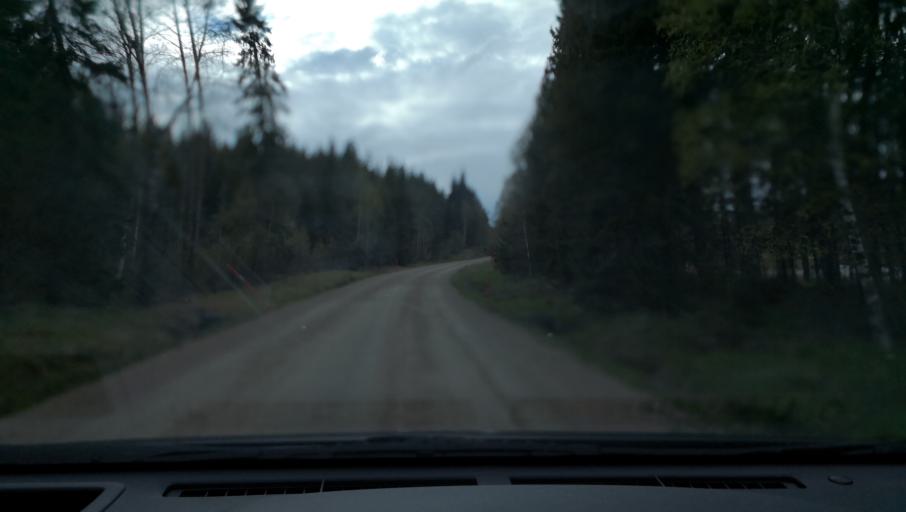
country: SE
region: Vaestmanland
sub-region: Fagersta Kommun
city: Fagersta
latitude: 60.1203
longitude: 15.7182
